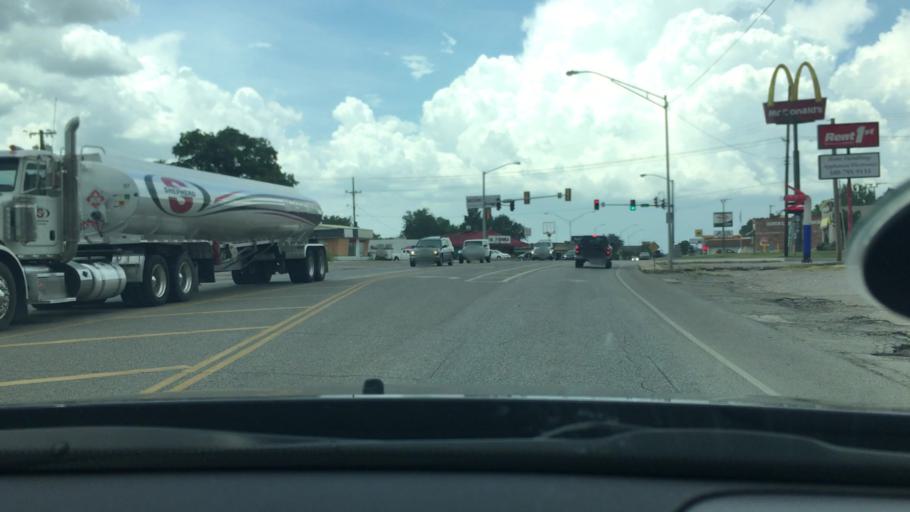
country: US
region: Oklahoma
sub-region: Marshall County
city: Madill
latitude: 34.0847
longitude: -96.7693
